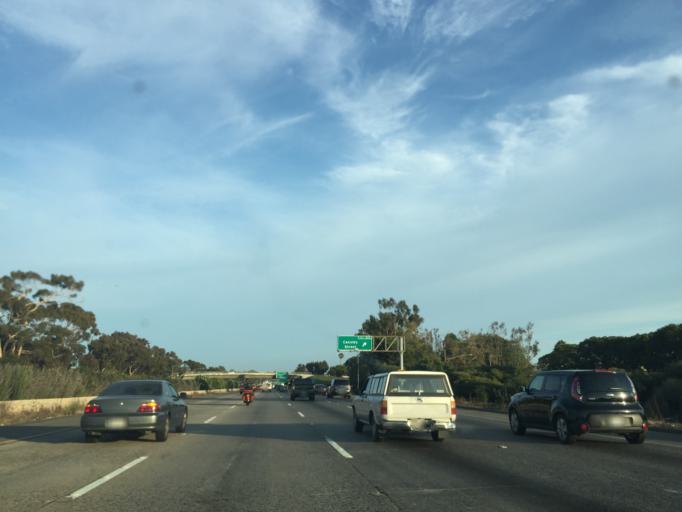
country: US
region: California
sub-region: San Diego County
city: Carlsbad
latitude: 33.1827
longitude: -117.3562
